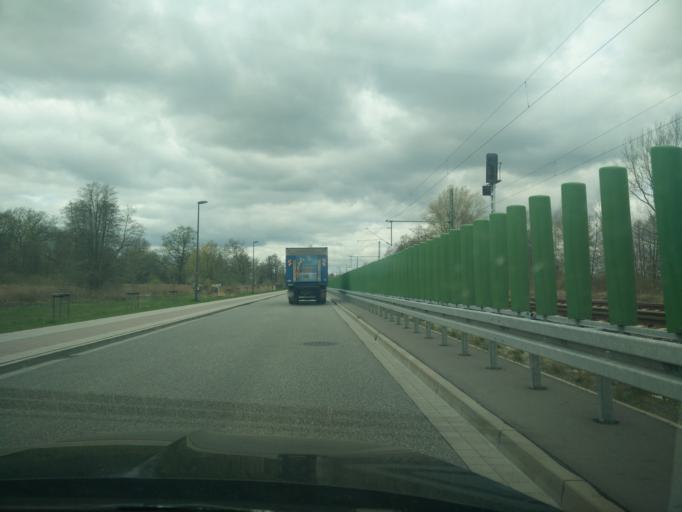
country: DE
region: Brandenburg
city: Bad Liebenwerda
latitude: 51.5160
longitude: 13.4076
